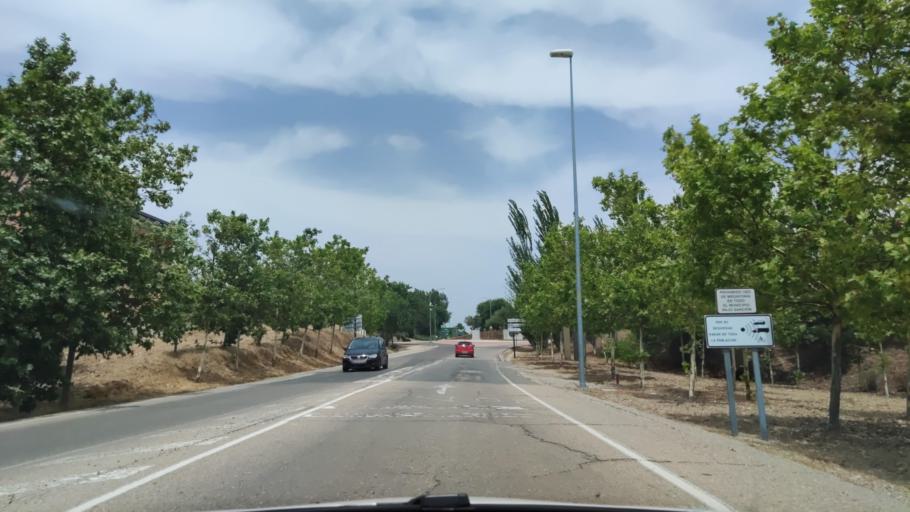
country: ES
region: Madrid
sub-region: Provincia de Madrid
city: Navalcarnero
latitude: 40.2800
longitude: -4.0262
